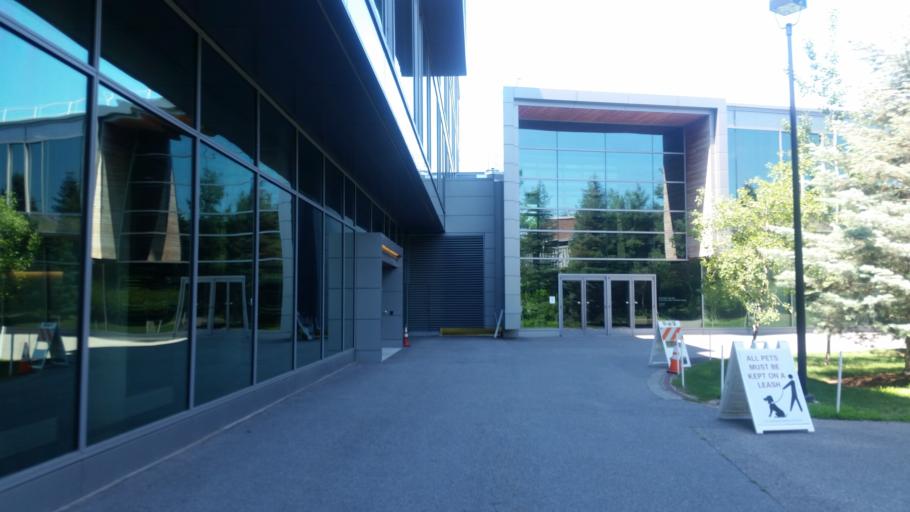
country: US
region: Massachusetts
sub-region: Middlesex County
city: Cambridge
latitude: 42.3800
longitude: -71.1152
